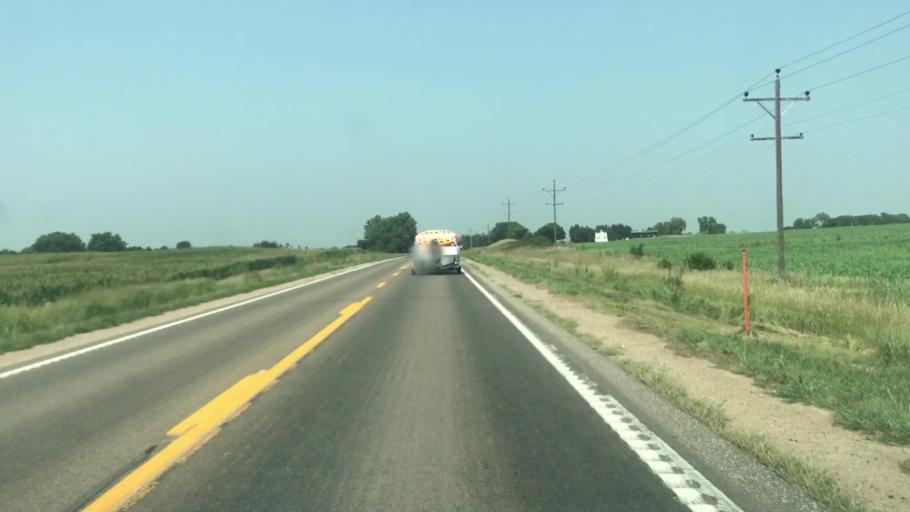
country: US
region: Nebraska
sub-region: Hall County
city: Wood River
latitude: 41.0148
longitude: -98.6073
